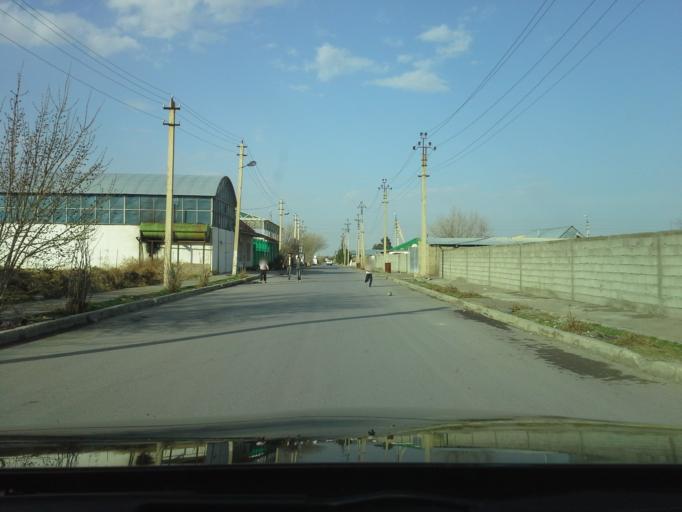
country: TM
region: Ahal
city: Abadan
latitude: 38.0197
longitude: 58.2347
